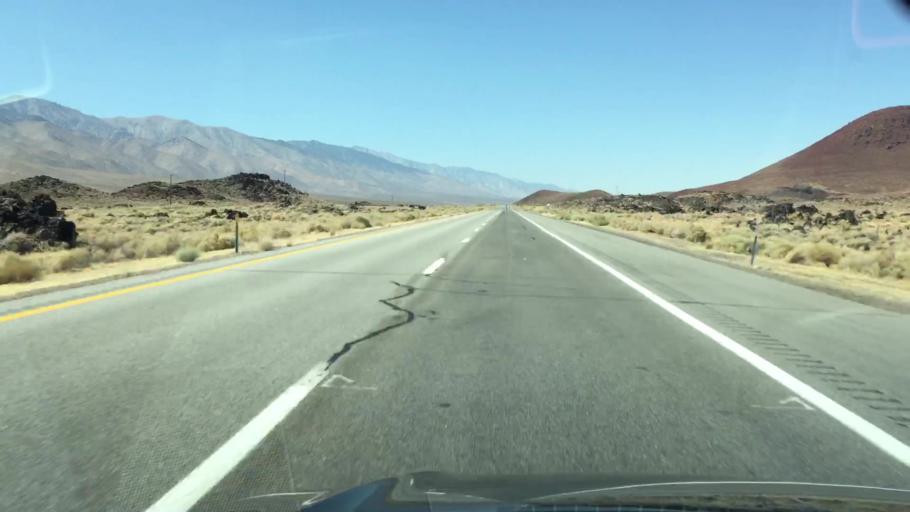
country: US
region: California
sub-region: Kern County
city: Inyokern
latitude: 35.9704
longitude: -117.9199
